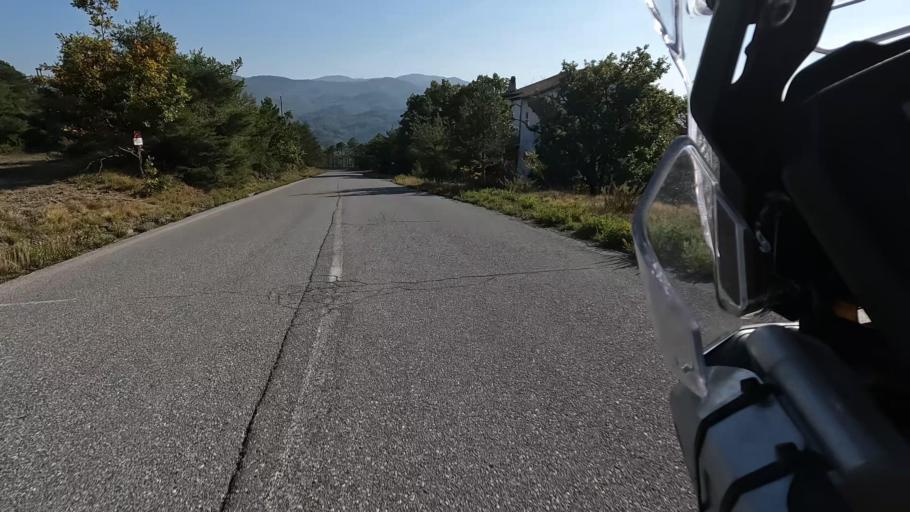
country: IT
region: Liguria
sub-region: Provincia di Savona
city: Sassello
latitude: 44.5058
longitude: 8.5357
